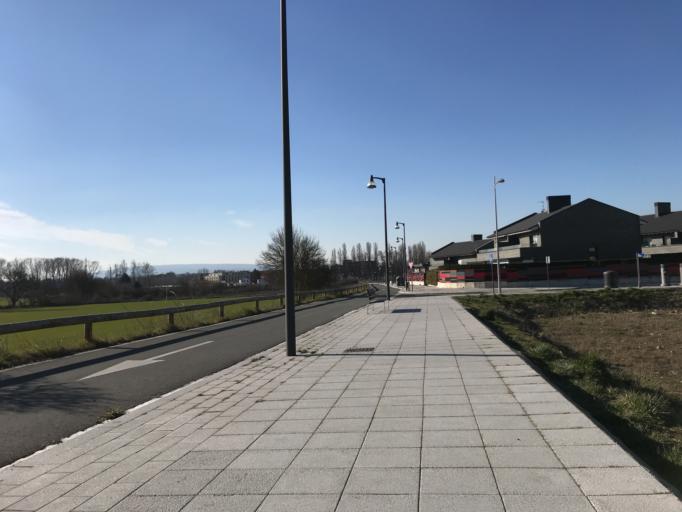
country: ES
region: Basque Country
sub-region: Provincia de Alava
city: Gasteiz / Vitoria
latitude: 42.8328
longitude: -2.6740
